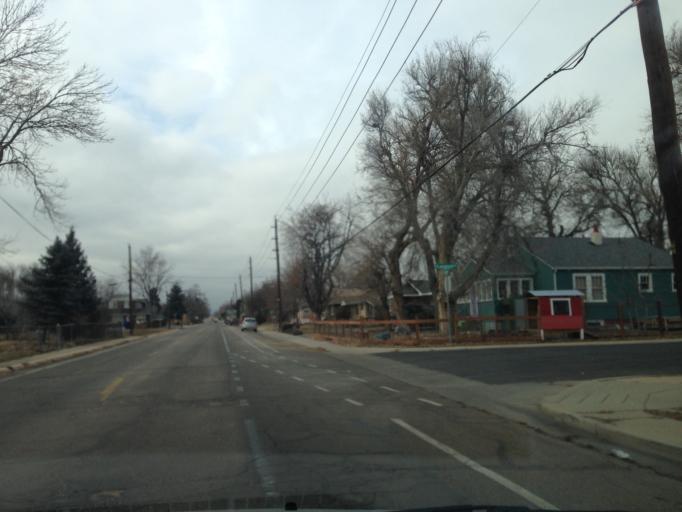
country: US
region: Colorado
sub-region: Boulder County
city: Lafayette
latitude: 39.9943
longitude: -105.0928
